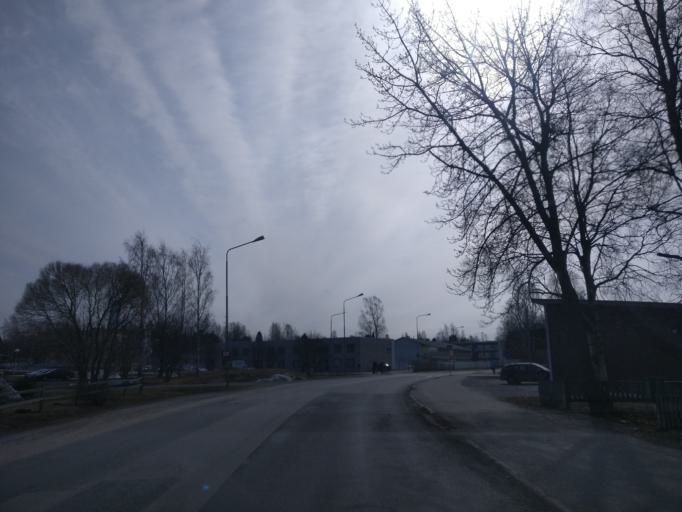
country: FI
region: Lapland
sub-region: Kemi-Tornio
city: Kemi
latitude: 65.7503
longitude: 24.5599
